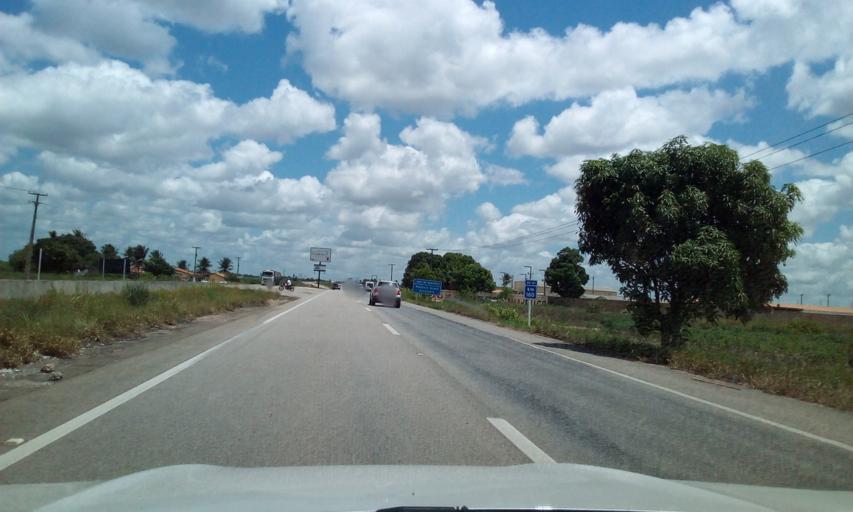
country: BR
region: Alagoas
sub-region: Junqueiro
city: Junqueiro
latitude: -9.8883
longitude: -36.3998
